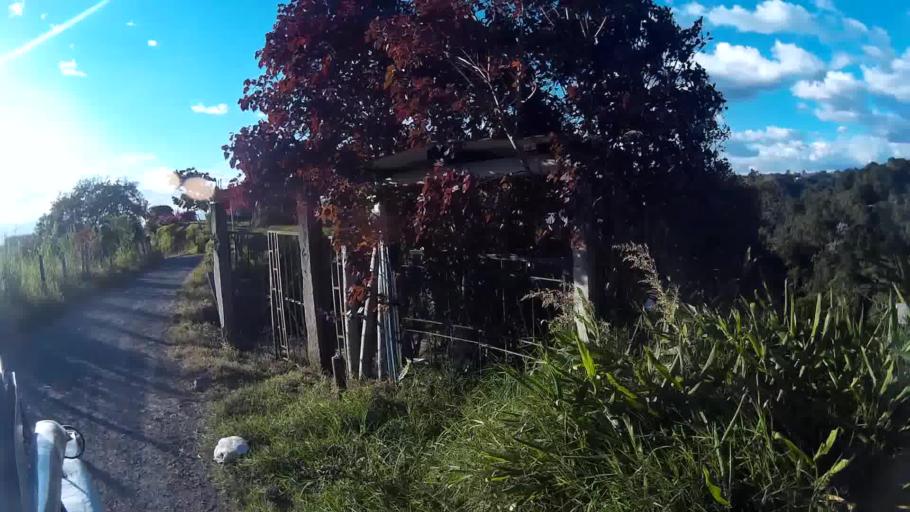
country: CO
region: Quindio
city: Filandia
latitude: 4.7245
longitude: -75.6805
